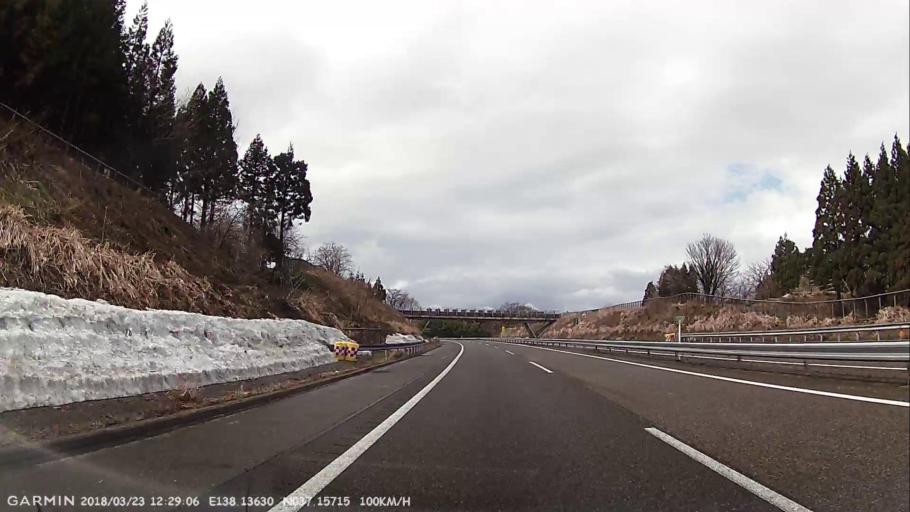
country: JP
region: Niigata
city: Joetsu
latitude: 37.1573
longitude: 138.1361
